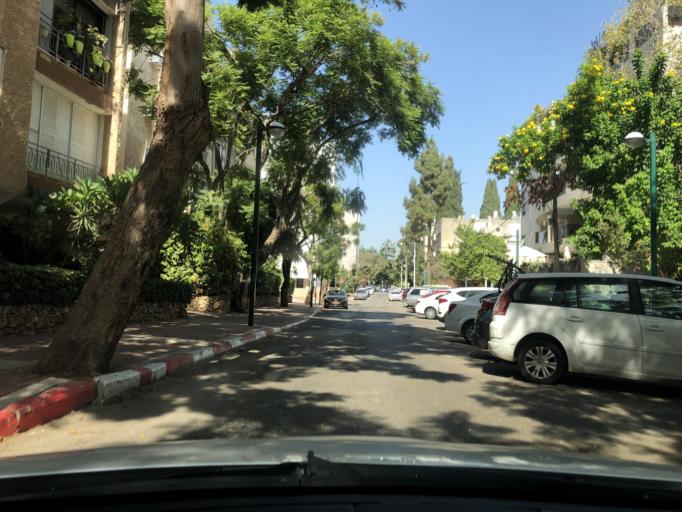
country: IL
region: Central District
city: Kfar Saba
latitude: 32.1739
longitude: 34.8950
